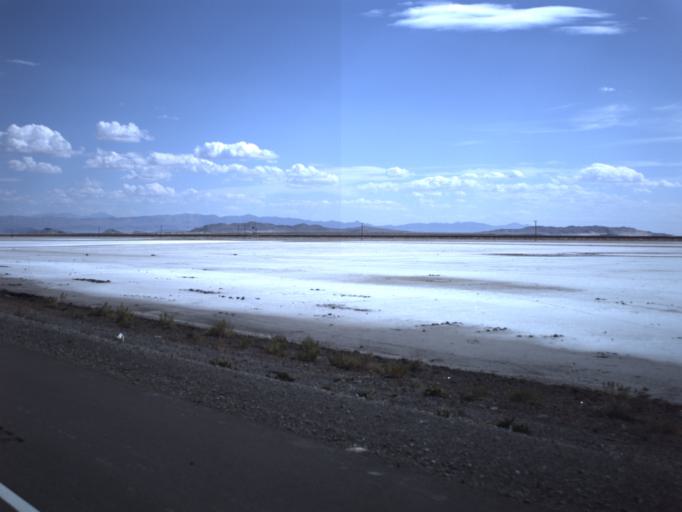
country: US
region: Utah
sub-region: Tooele County
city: Wendover
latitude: 40.7285
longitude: -113.3973
